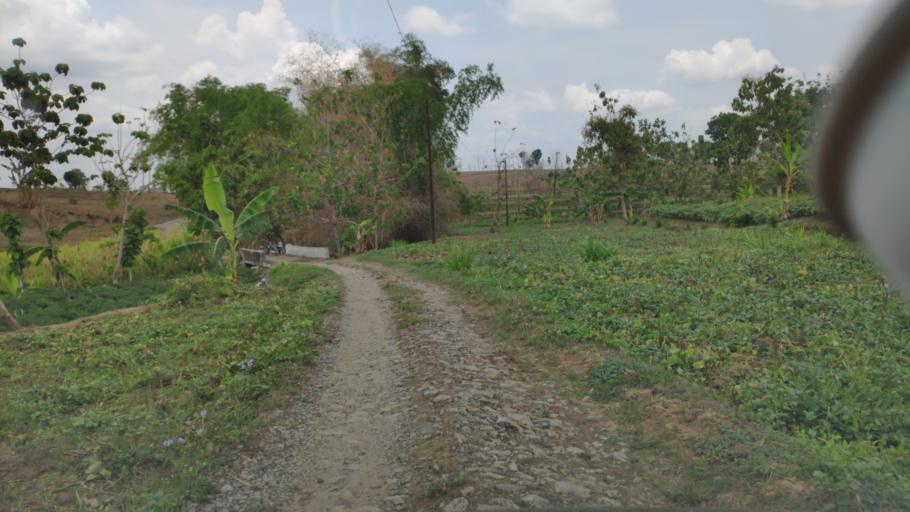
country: ID
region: Central Java
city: Gumiring
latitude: -7.0483
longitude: 111.3932
